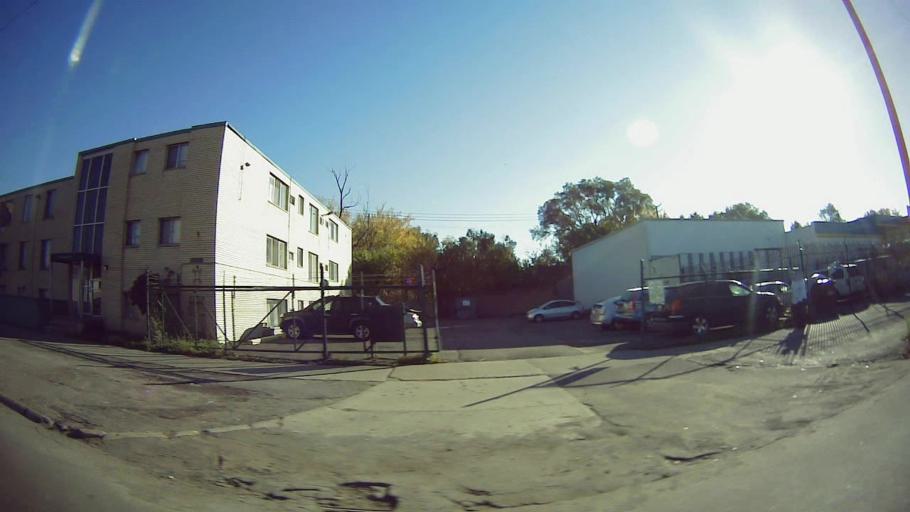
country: US
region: Michigan
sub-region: Wayne County
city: Dearborn
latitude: 42.3743
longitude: -83.1975
